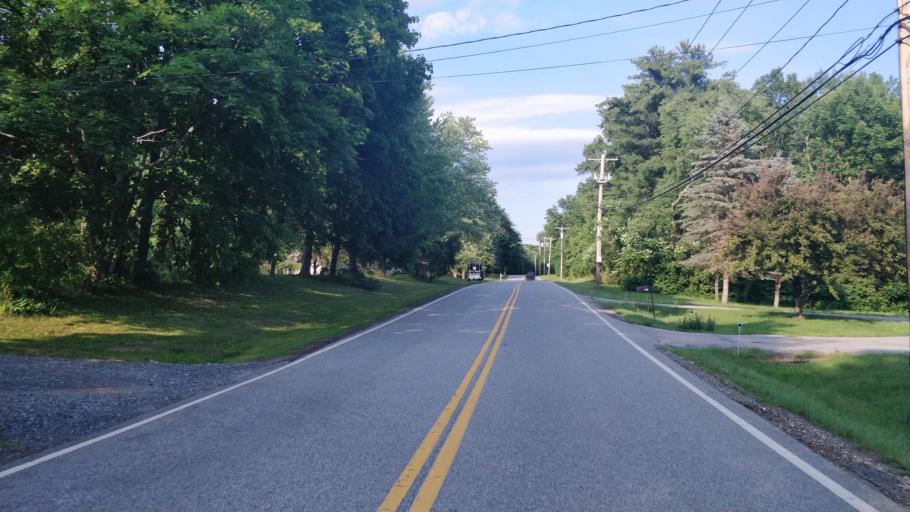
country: US
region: New York
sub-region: Saratoga County
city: North Ballston Spa
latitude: 43.0208
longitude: -73.8177
